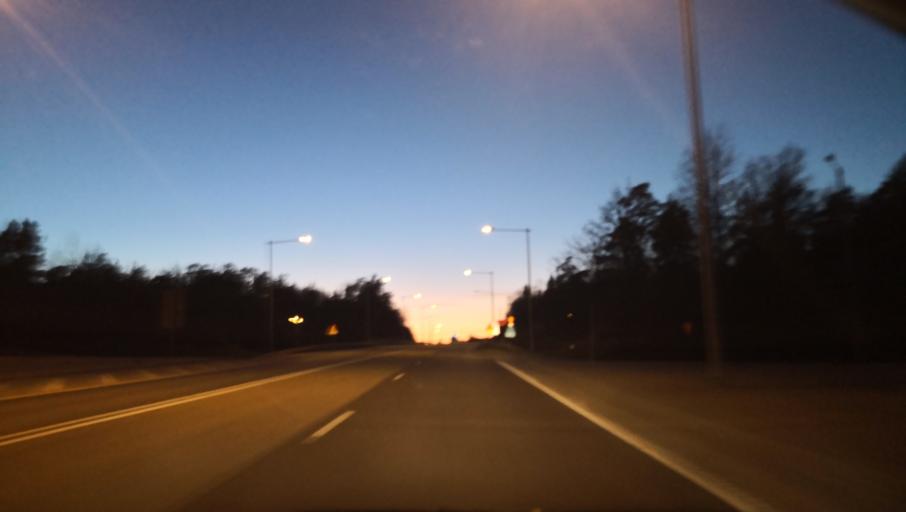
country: SE
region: Stockholm
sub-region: Nynashamns Kommun
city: Nynashamn
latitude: 58.9196
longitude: 17.9530
